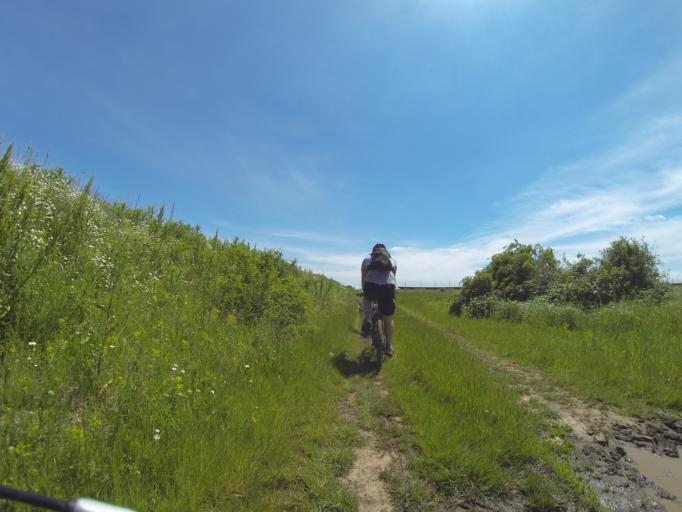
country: RO
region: Dolj
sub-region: Comuna Leu
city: Zanoaga
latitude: 44.1824
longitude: 24.0728
